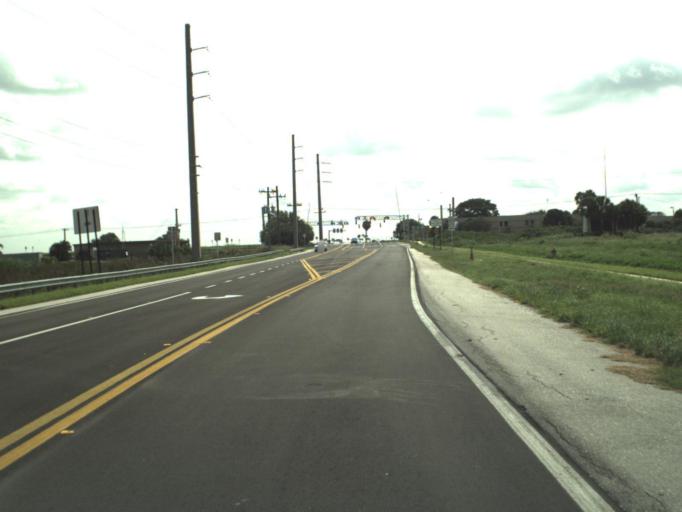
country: US
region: Florida
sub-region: Palm Beach County
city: Belle Glade
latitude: 26.7257
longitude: -80.6699
